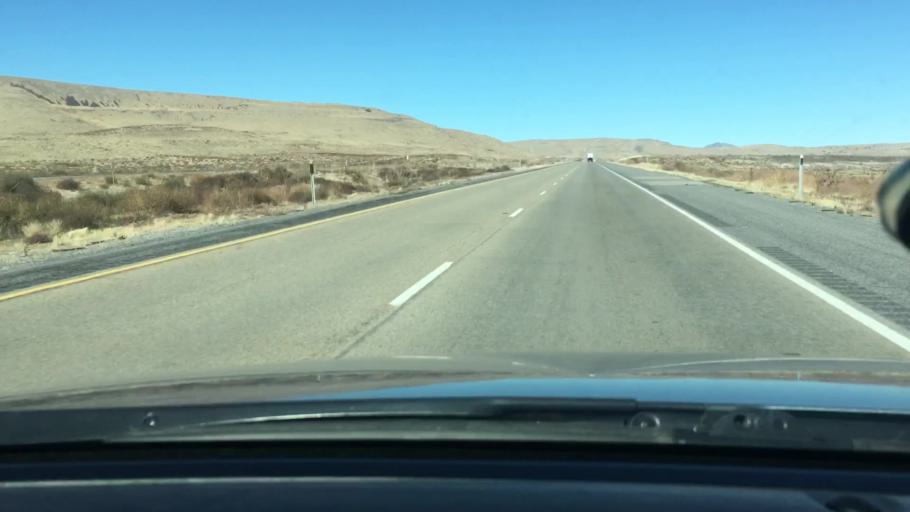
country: US
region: Utah
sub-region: Tooele County
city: Grantsville
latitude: 40.8088
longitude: -112.8650
